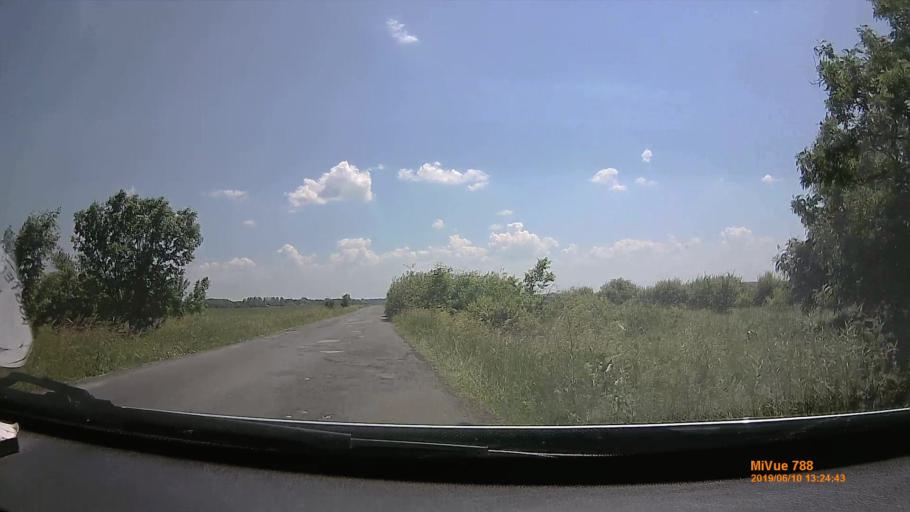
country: HU
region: Borsod-Abauj-Zemplen
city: Tiszaluc
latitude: 48.0197
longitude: 21.1042
